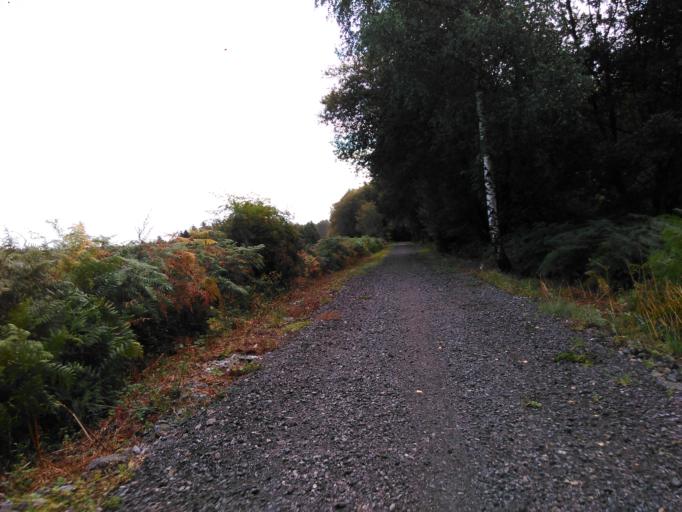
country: BE
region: Wallonia
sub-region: Province du Luxembourg
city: Neufchateau
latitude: 49.9061
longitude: 5.4752
